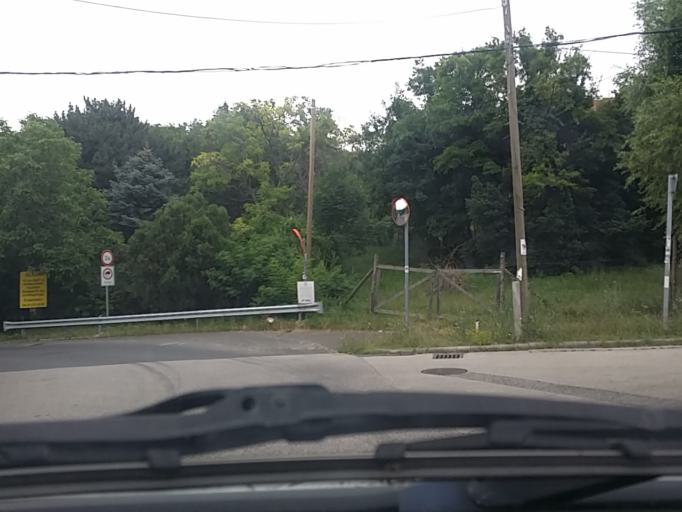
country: HU
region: Pest
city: Urom
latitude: 47.5885
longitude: 19.0340
